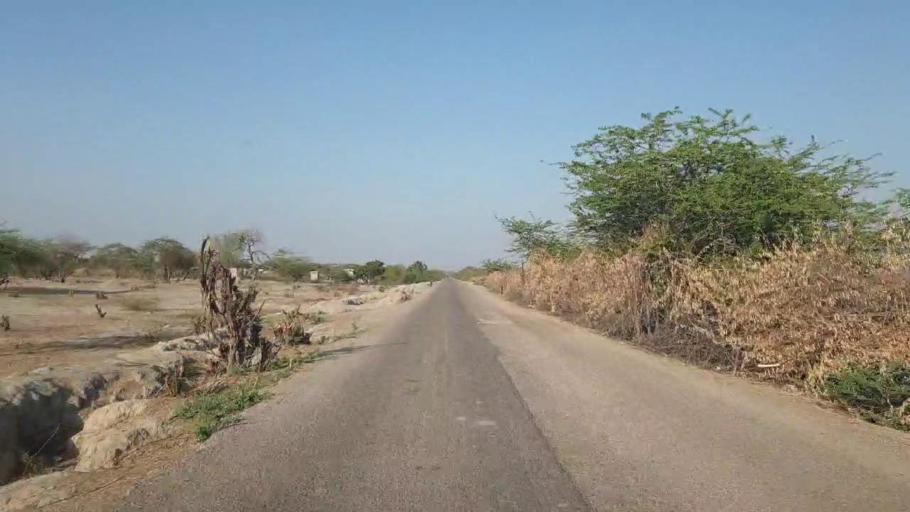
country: PK
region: Sindh
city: Chor
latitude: 25.5581
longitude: 69.7947
